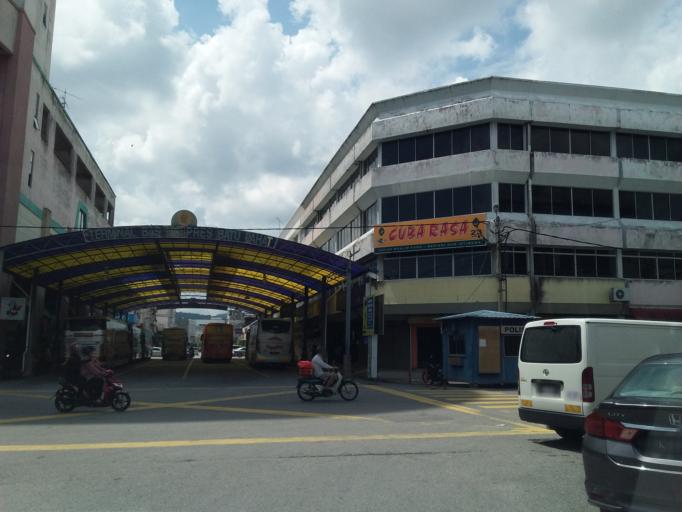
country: MY
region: Johor
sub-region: Daerah Batu Pahat
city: Batu Pahat
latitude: 1.8529
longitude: 102.9260
